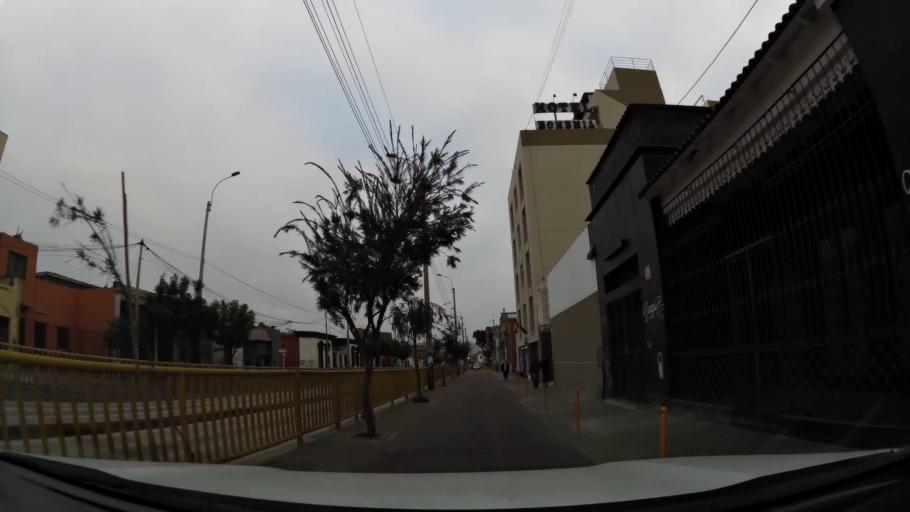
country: PE
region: Lima
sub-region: Lima
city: Surco
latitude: -12.1443
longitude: -77.0188
